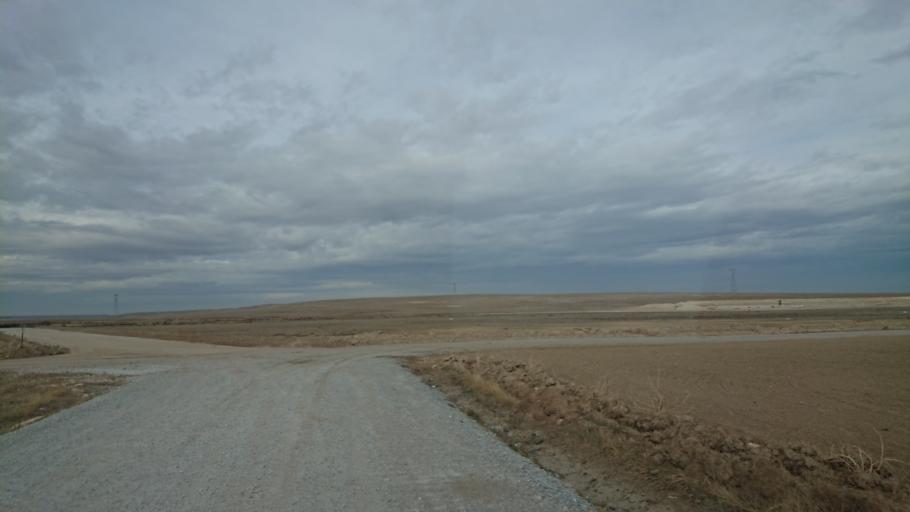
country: TR
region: Aksaray
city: Sultanhani
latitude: 38.1337
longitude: 33.5516
